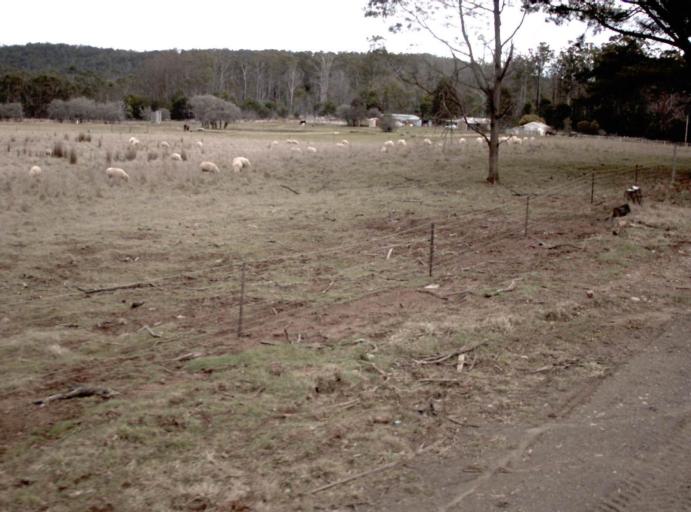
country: AU
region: Tasmania
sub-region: Launceston
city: Newstead
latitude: -41.3655
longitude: 147.2478
